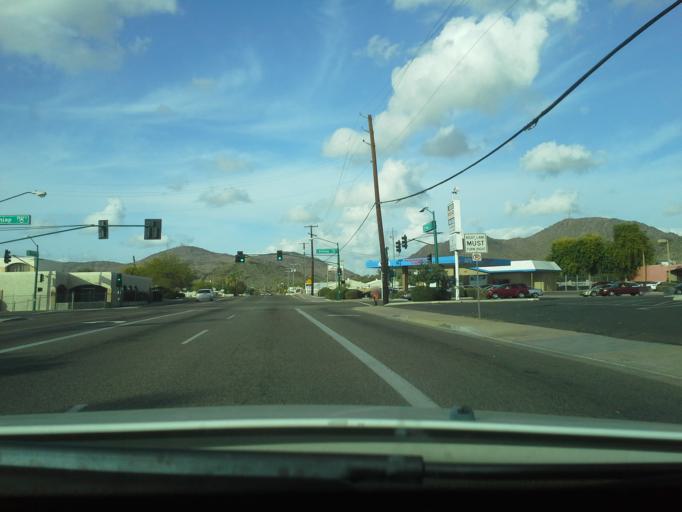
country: US
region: Arizona
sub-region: Maricopa County
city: Glendale
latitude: 33.5669
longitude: -112.0825
